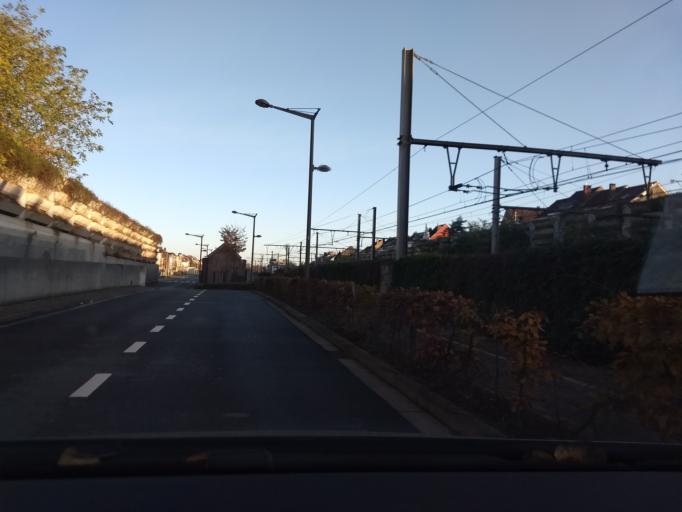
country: BE
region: Wallonia
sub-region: Province du Brabant Wallon
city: Braine-l'Alleud
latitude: 50.6798
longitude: 4.3749
